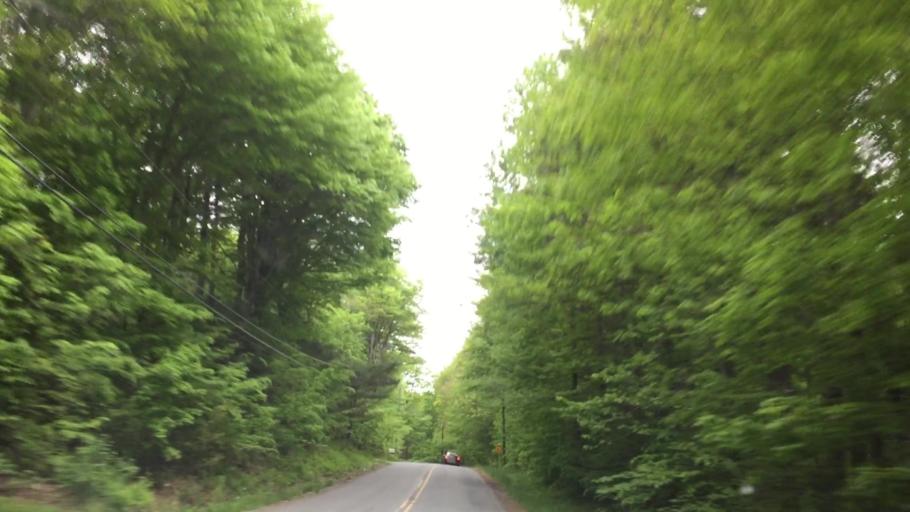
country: US
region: Massachusetts
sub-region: Berkshire County
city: Becket
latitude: 42.2795
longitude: -73.0444
